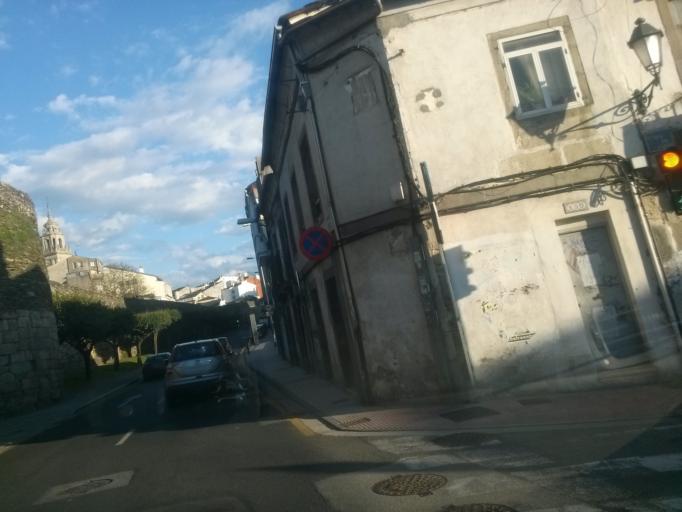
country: ES
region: Galicia
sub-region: Provincia de Lugo
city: Lugo
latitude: 43.0101
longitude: -7.5609
